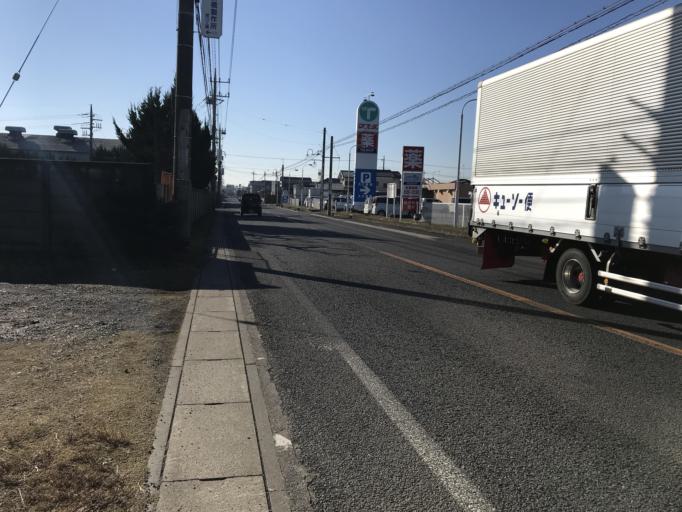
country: JP
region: Ibaraki
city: Sakai
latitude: 36.1941
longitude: 139.8119
